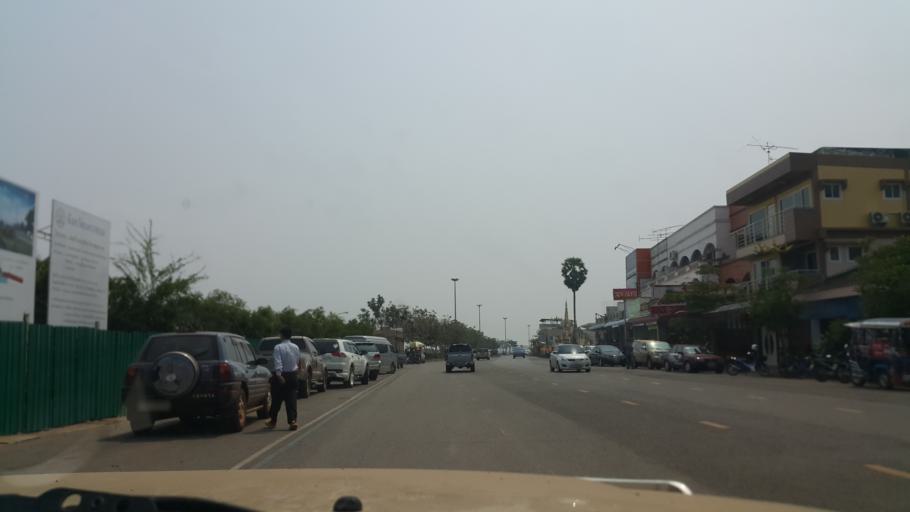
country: TH
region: Nakhon Phanom
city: Nakhon Phanom
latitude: 17.3987
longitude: 104.7905
